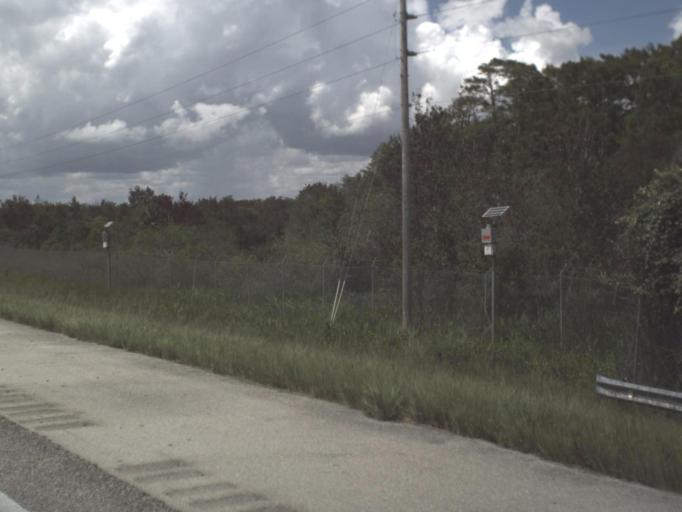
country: US
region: Florida
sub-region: Collier County
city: Immokalee
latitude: 26.1558
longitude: -81.2600
